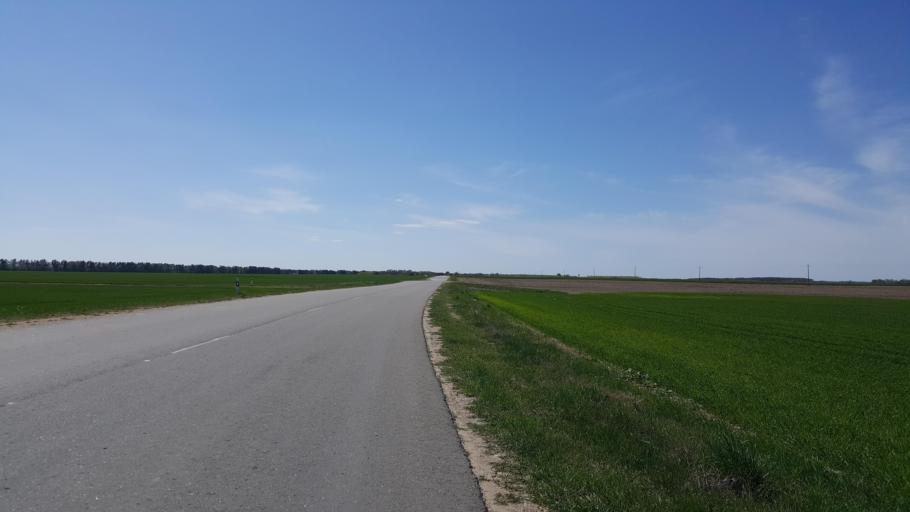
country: BY
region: Brest
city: Vysokaye
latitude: 52.3521
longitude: 23.4845
